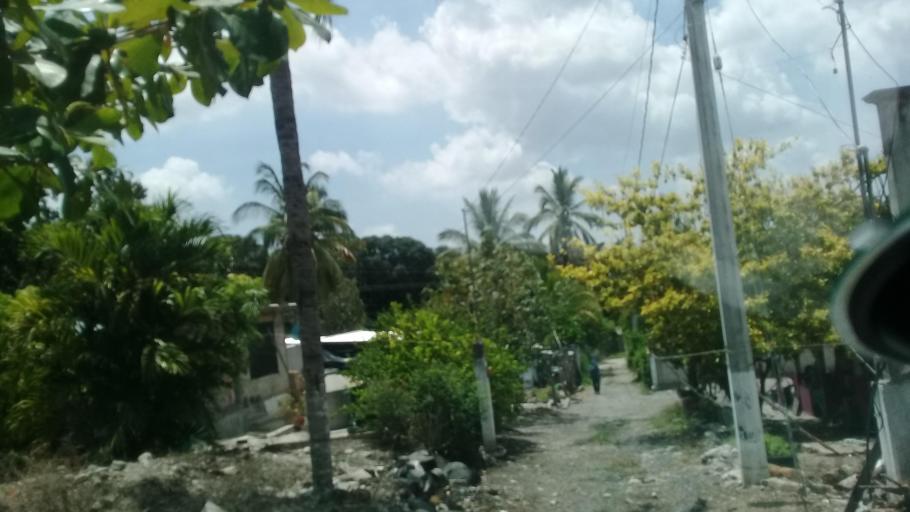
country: MX
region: Veracruz
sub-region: Emiliano Zapata
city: Plan del Rio
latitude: 19.4056
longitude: -96.6529
